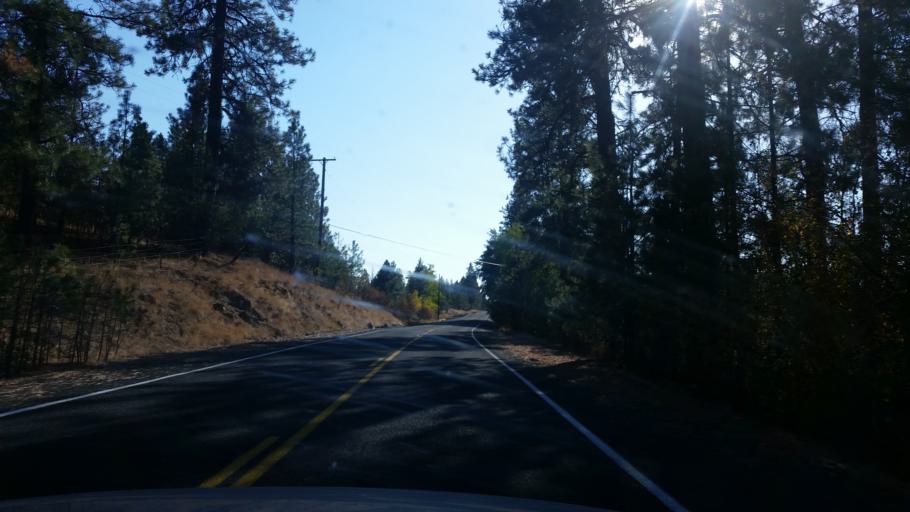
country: US
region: Washington
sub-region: Spokane County
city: Cheney
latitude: 47.4082
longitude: -117.6539
